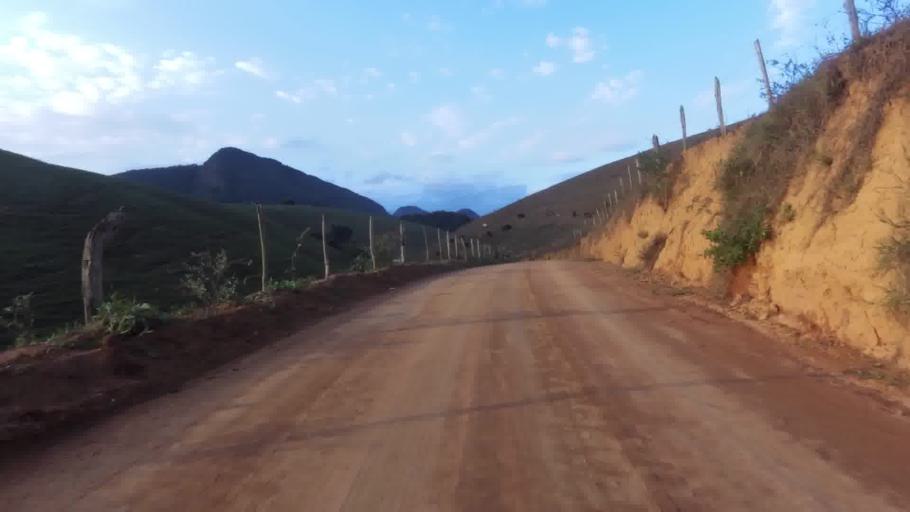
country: BR
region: Espirito Santo
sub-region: Alfredo Chaves
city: Alfredo Chaves
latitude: -20.6934
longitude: -40.6324
